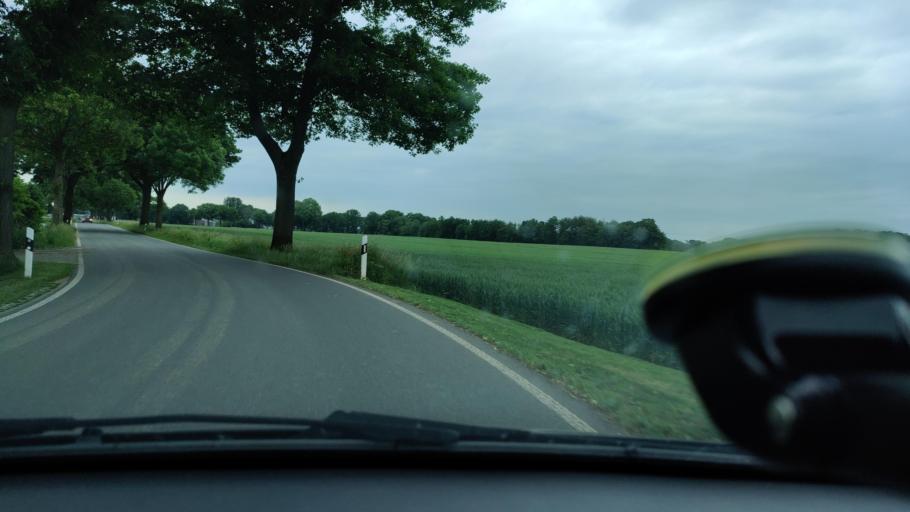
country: DE
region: North Rhine-Westphalia
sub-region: Regierungsbezirk Dusseldorf
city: Goch
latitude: 51.6813
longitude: 6.1065
